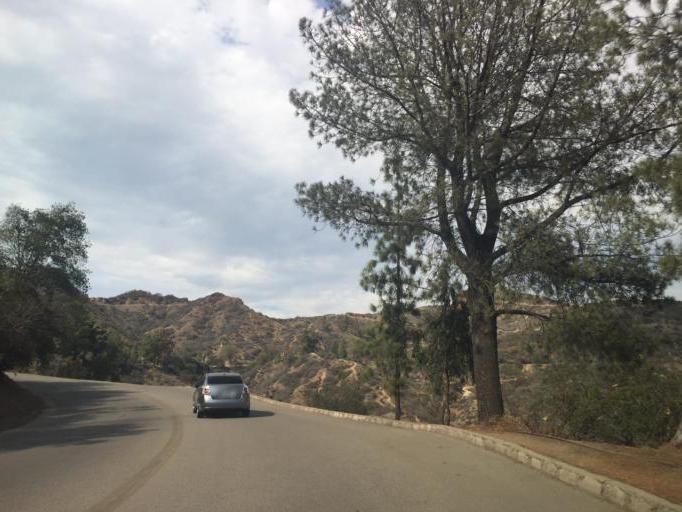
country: US
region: California
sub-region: Los Angeles County
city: Hollywood
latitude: 34.1190
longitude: -118.3079
